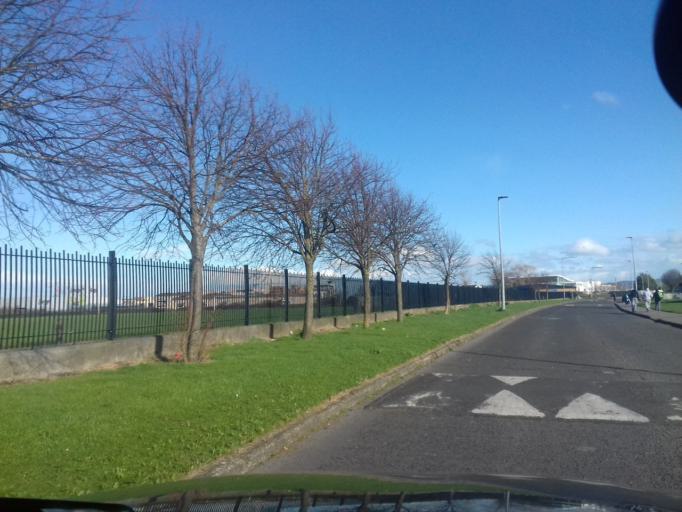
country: IE
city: Darndale
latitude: 53.4029
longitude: -6.1912
